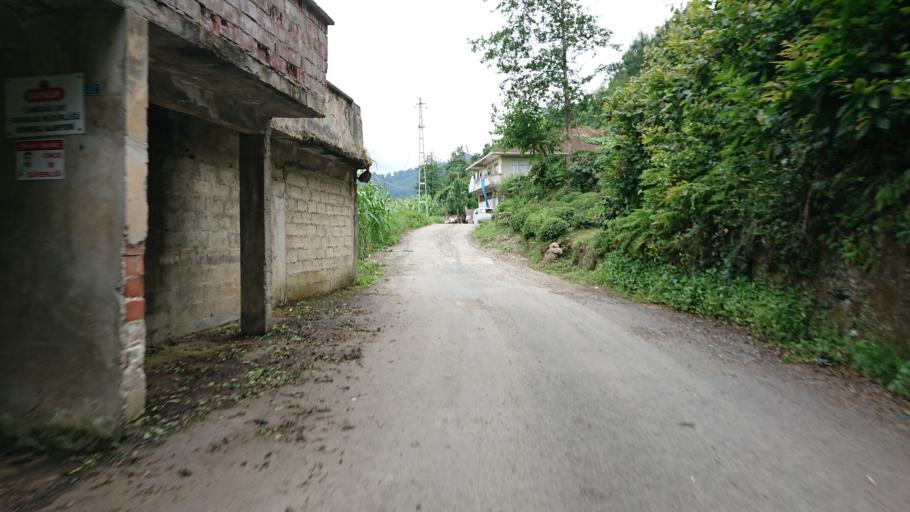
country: TR
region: Rize
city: Rize
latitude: 40.9705
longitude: 40.5157
